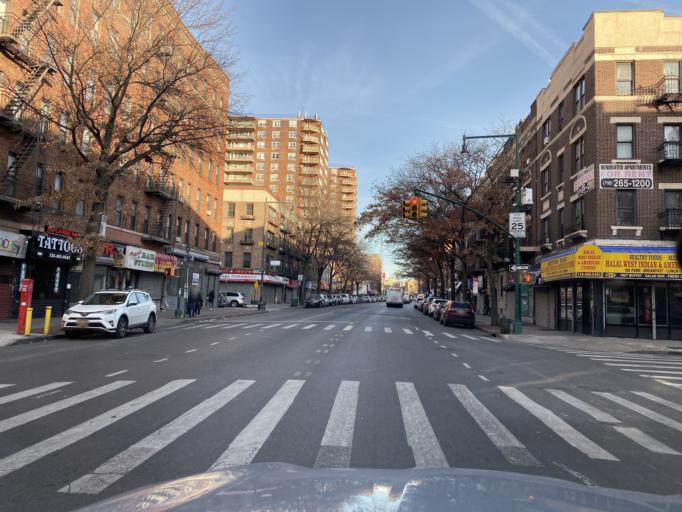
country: US
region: New York
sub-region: Kings County
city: Brooklyn
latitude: 40.6579
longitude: -73.9604
